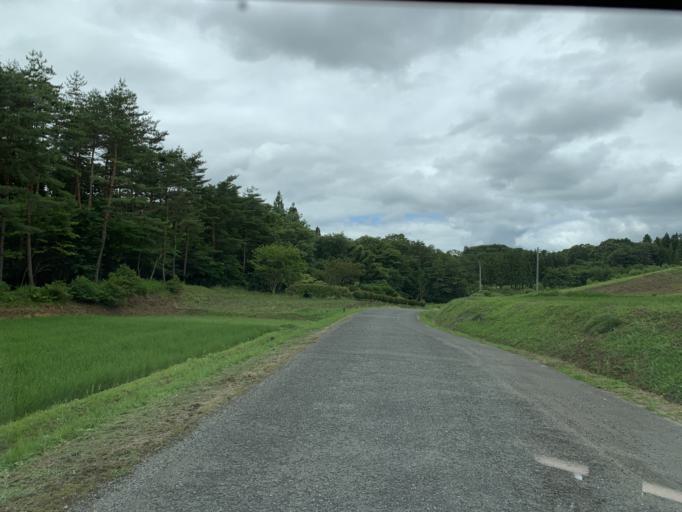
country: JP
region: Iwate
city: Ichinoseki
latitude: 38.9086
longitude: 141.0733
